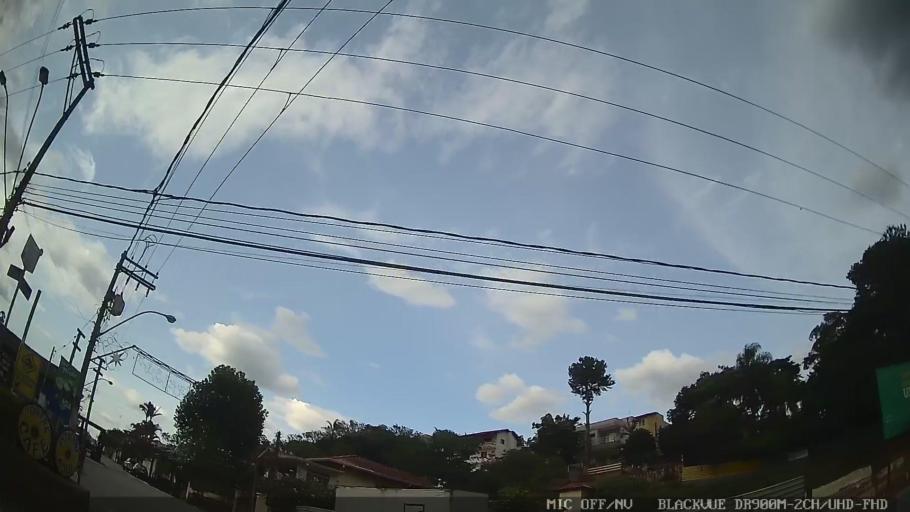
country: BR
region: Sao Paulo
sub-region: Itatiba
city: Itatiba
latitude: -22.8846
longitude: -46.7917
